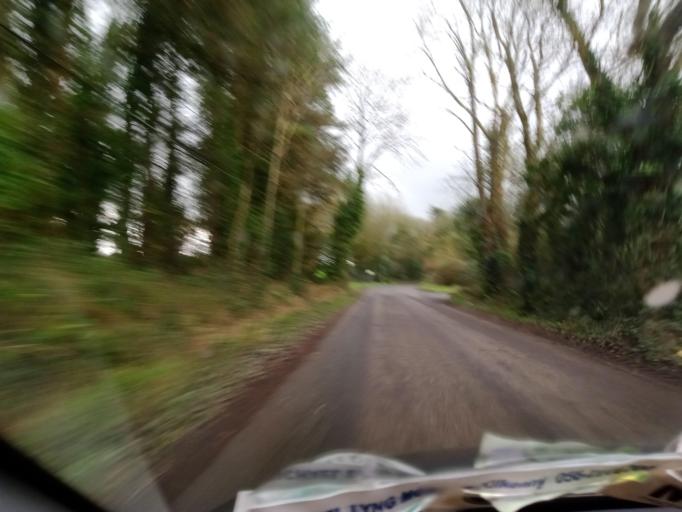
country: IE
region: Munster
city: Fethard
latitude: 52.5523
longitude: -7.7613
